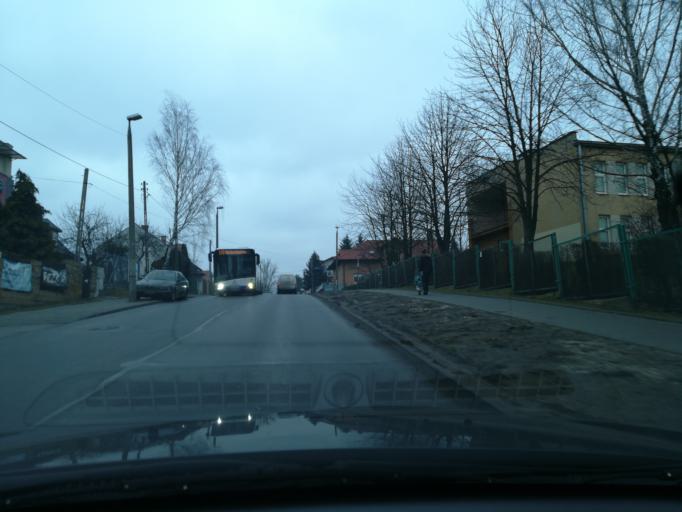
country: PL
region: Lesser Poland Voivodeship
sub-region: Krakow
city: Krakow
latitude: 50.0172
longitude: 19.9510
